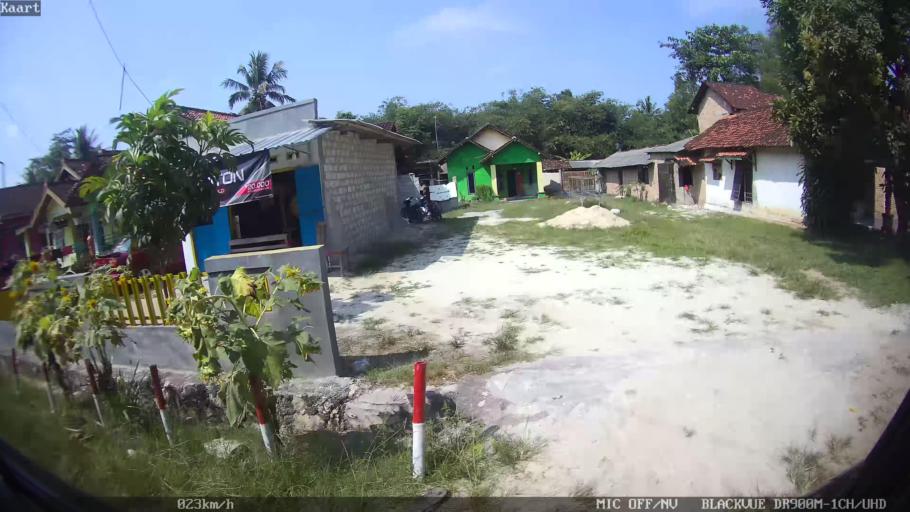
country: ID
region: Lampung
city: Natar
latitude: -5.2534
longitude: 105.1963
